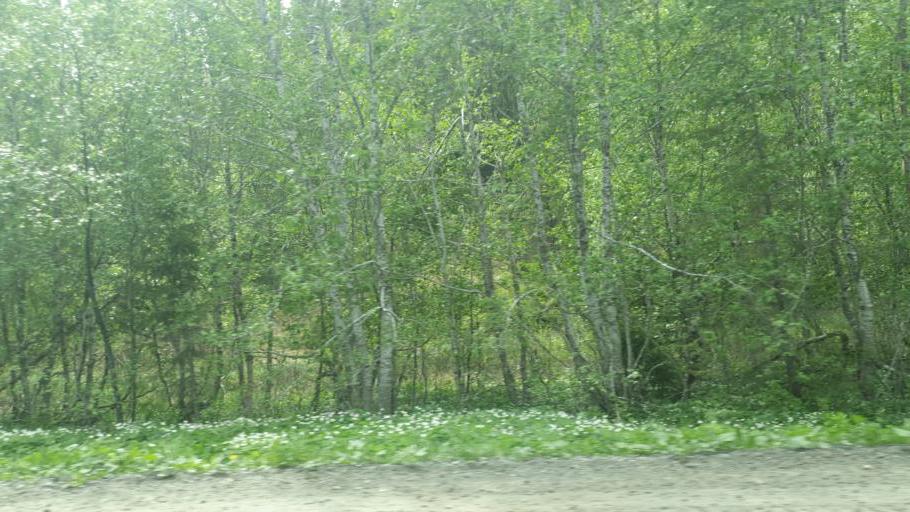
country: NO
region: Nord-Trondelag
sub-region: Leksvik
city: Leksvik
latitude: 63.6935
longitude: 10.4485
